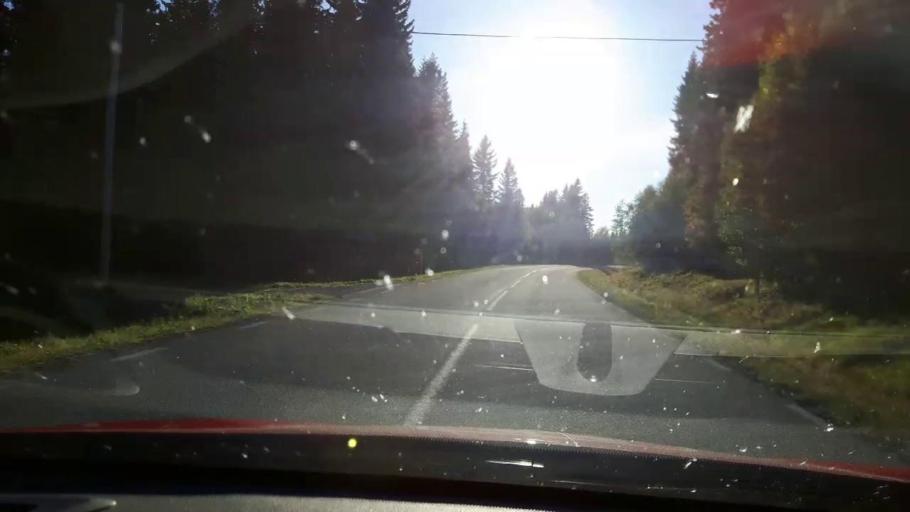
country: SE
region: Jaemtland
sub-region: OEstersunds Kommun
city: Lit
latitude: 63.8064
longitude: 14.7501
